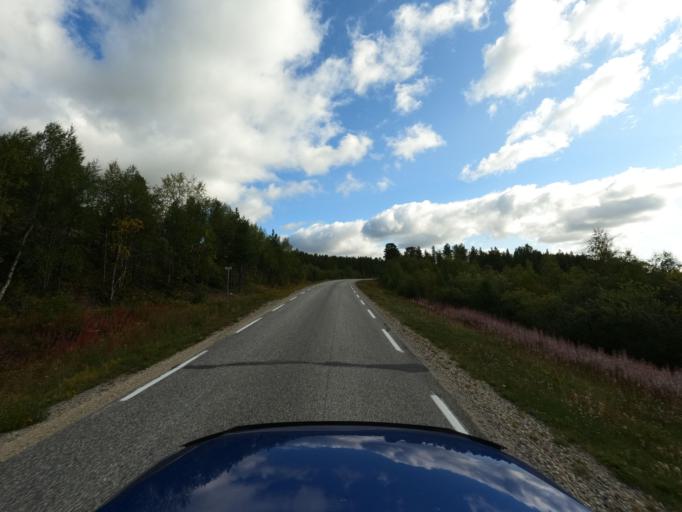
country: NO
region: Finnmark Fylke
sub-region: Karasjok
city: Karasjohka
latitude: 69.4438
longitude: 25.2421
